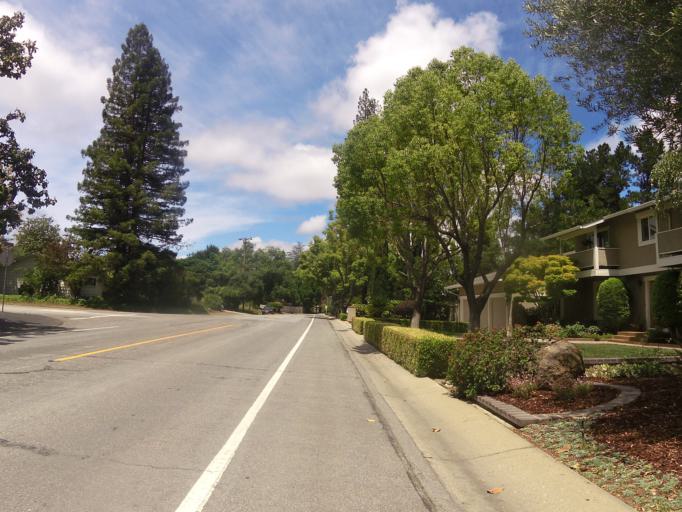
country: US
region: California
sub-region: Santa Clara County
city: Loyola
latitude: 37.3488
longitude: -122.0831
